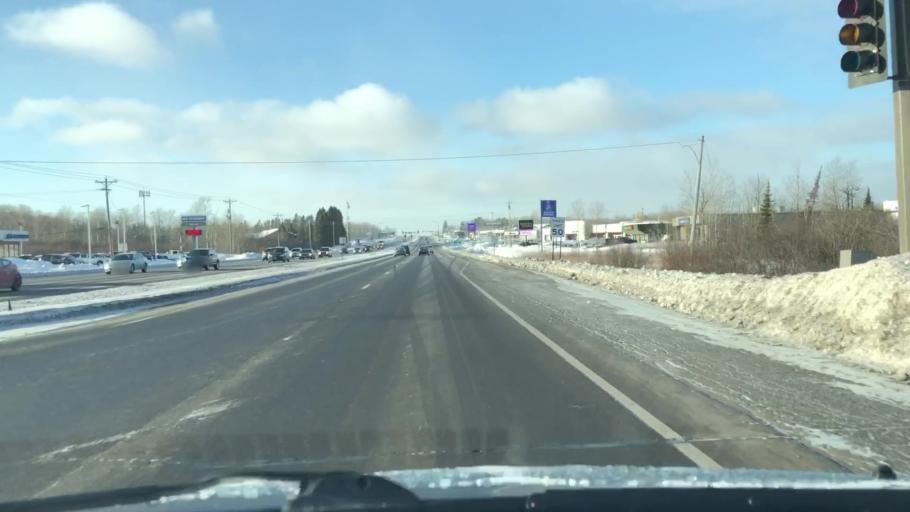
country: US
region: Minnesota
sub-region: Saint Louis County
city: Hermantown
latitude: 46.8192
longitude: -92.1818
